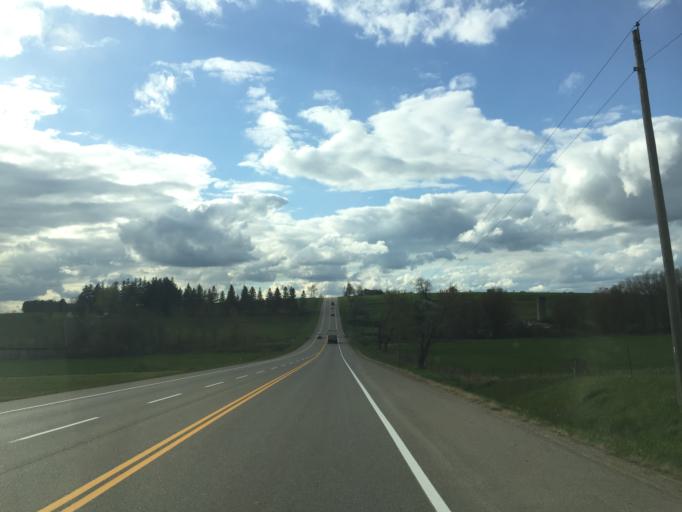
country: CA
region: Ontario
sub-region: Wellington County
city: Guelph
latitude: 43.5193
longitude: -80.3239
